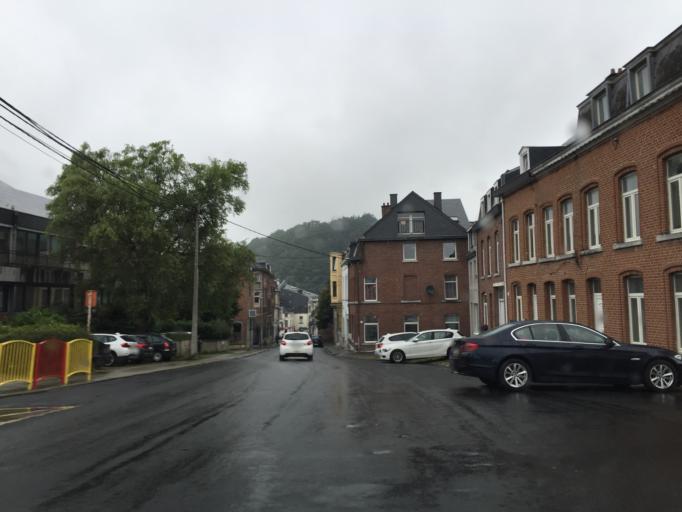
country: BE
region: Wallonia
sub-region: Province de Liege
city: Spa
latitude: 50.4896
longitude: 5.8677
